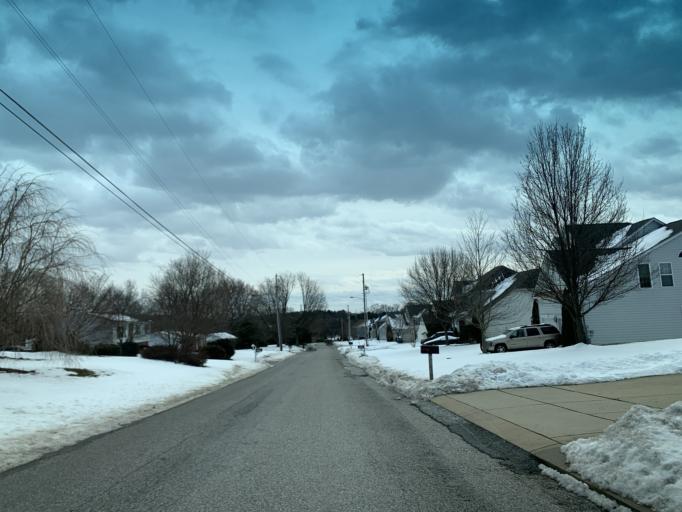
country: US
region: Pennsylvania
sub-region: York County
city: Shrewsbury
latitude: 39.7528
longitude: -76.6644
